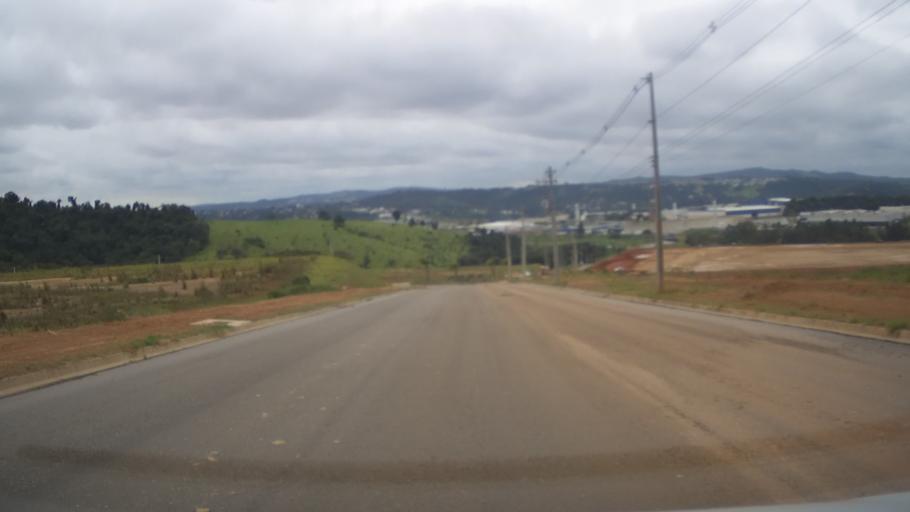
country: BR
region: Sao Paulo
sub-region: Vinhedo
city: Vinhedo
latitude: -23.0767
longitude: -47.0106
